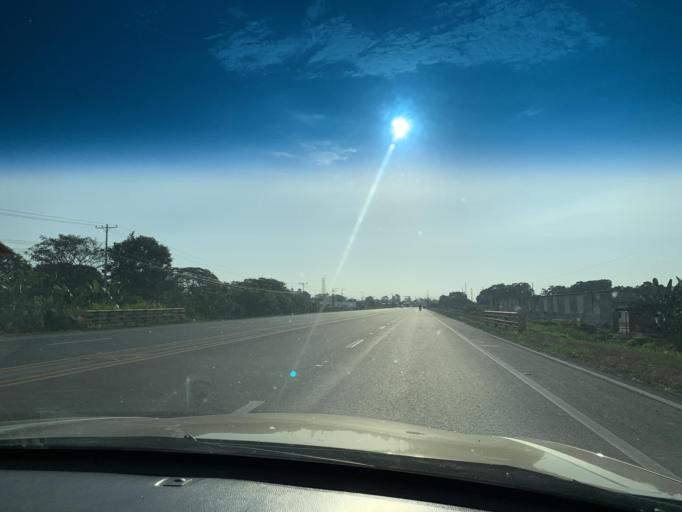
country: EC
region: Guayas
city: Yaguachi Nuevo
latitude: -2.2543
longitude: -79.6223
